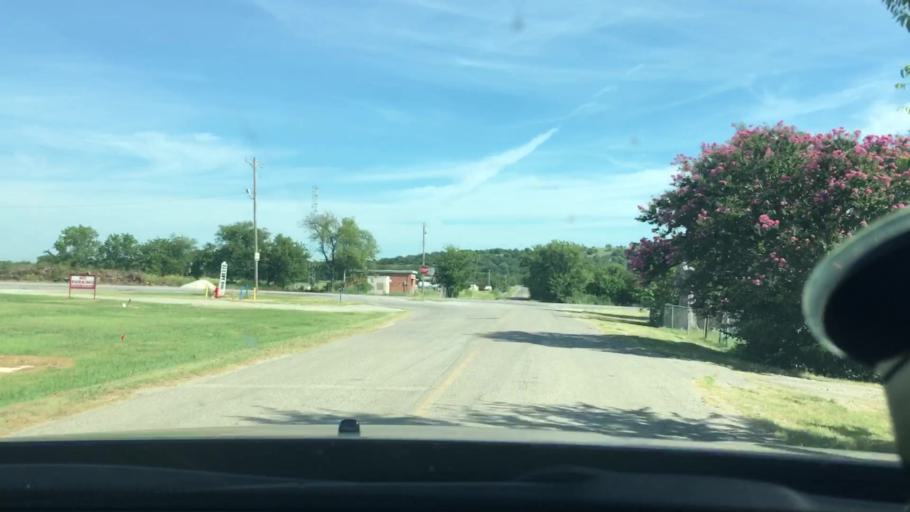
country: US
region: Oklahoma
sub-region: Carter County
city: Lone Grove
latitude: 34.3319
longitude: -97.2825
